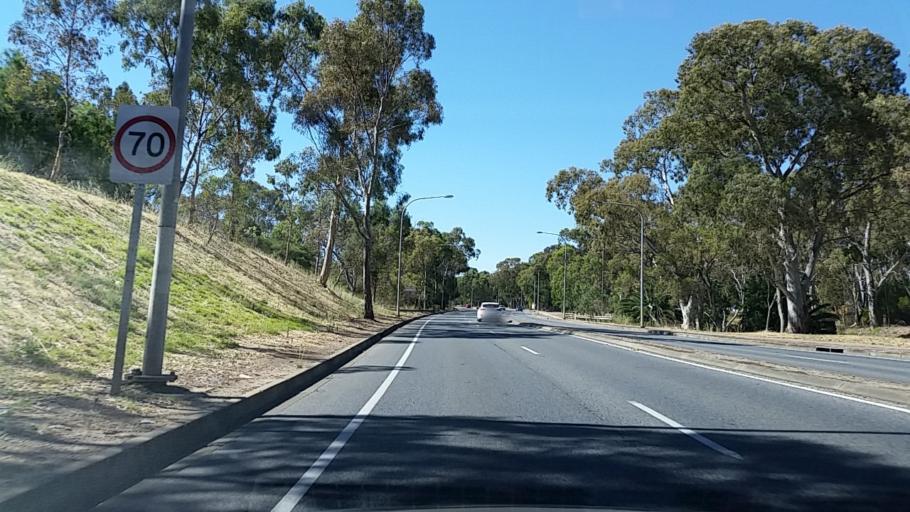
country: AU
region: South Australia
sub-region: Tea Tree Gully
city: Hope Valley
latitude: -34.8201
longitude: 138.6953
